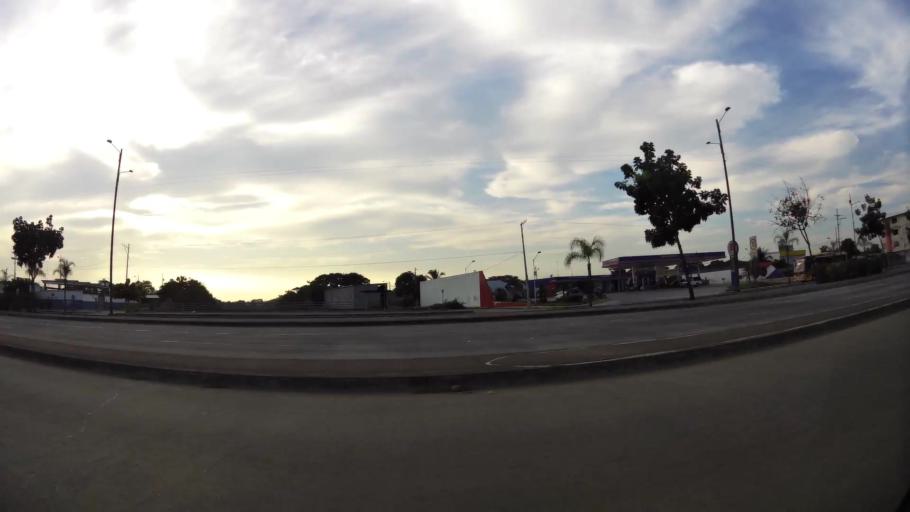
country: EC
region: Guayas
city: Eloy Alfaro
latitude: -2.0828
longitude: -79.8970
